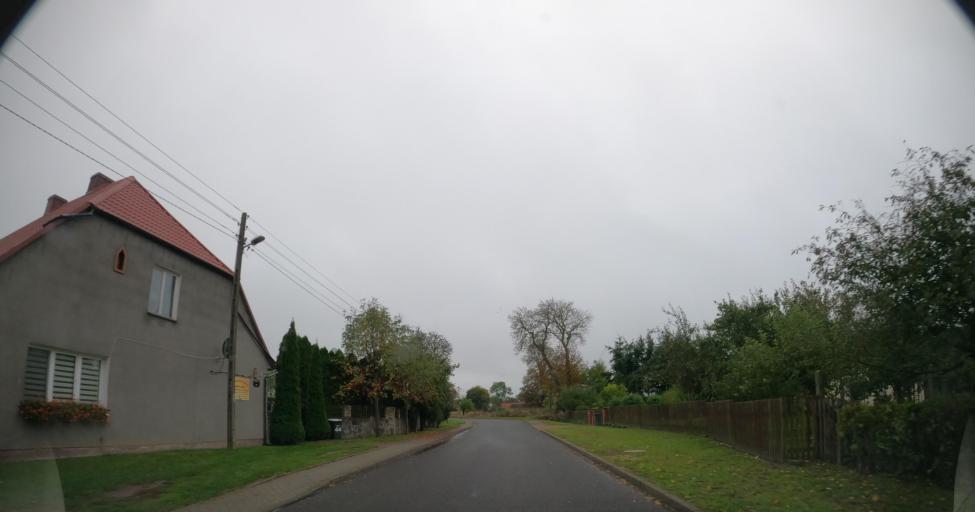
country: PL
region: West Pomeranian Voivodeship
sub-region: Powiat pyrzycki
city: Kozielice
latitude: 53.0944
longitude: 14.7683
